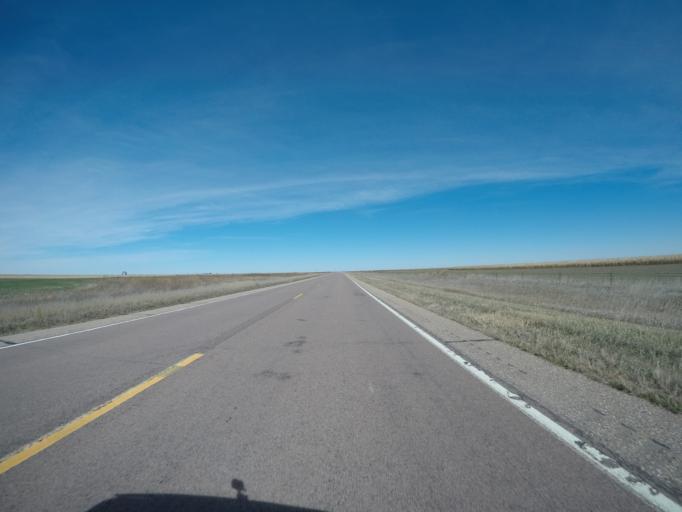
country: US
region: Colorado
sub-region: Kit Carson County
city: Burlington
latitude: 39.6775
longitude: -102.4140
